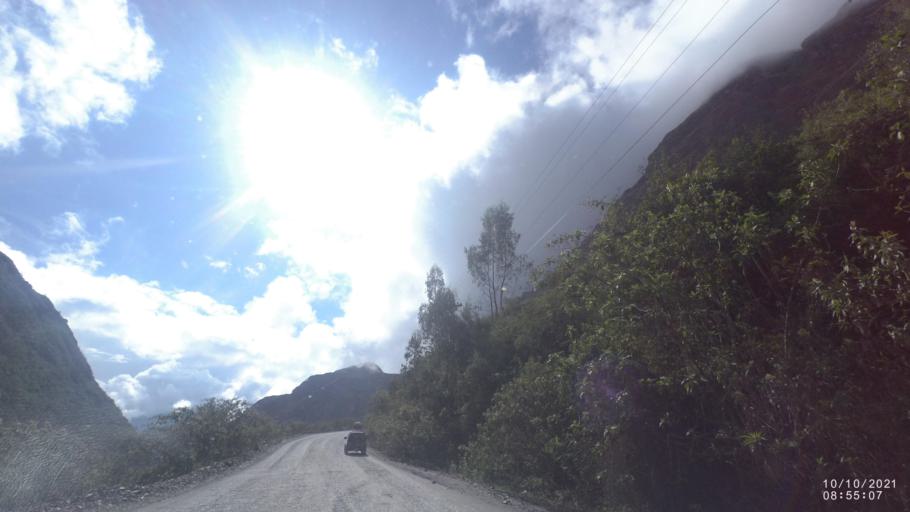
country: BO
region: La Paz
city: Quime
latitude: -16.9875
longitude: -67.2395
